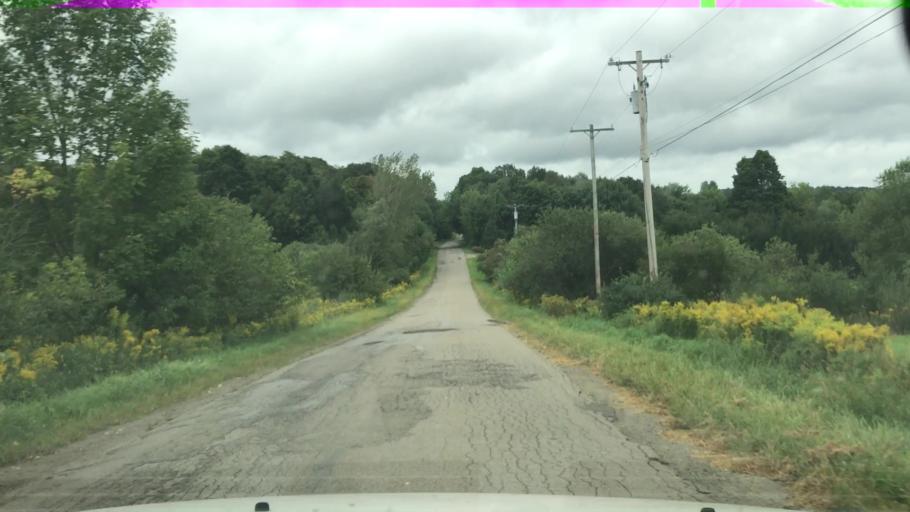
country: US
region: New York
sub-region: Cattaraugus County
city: Little Valley
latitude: 42.3286
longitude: -78.7244
